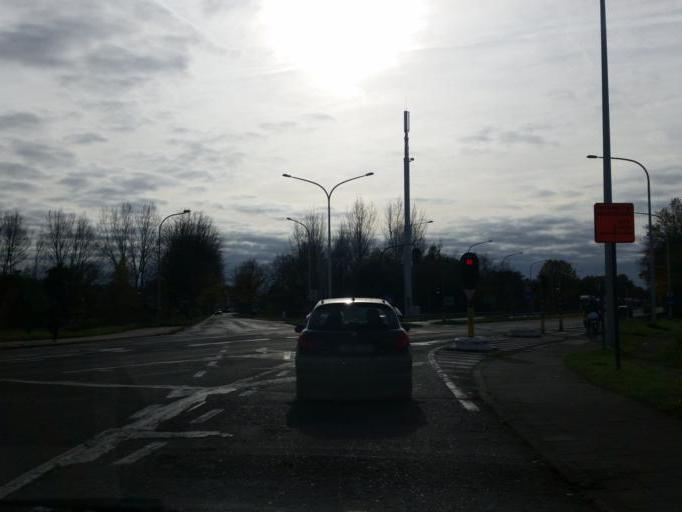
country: BE
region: Flanders
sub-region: Provincie Antwerpen
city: Edegem
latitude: 51.1458
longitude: 4.4465
